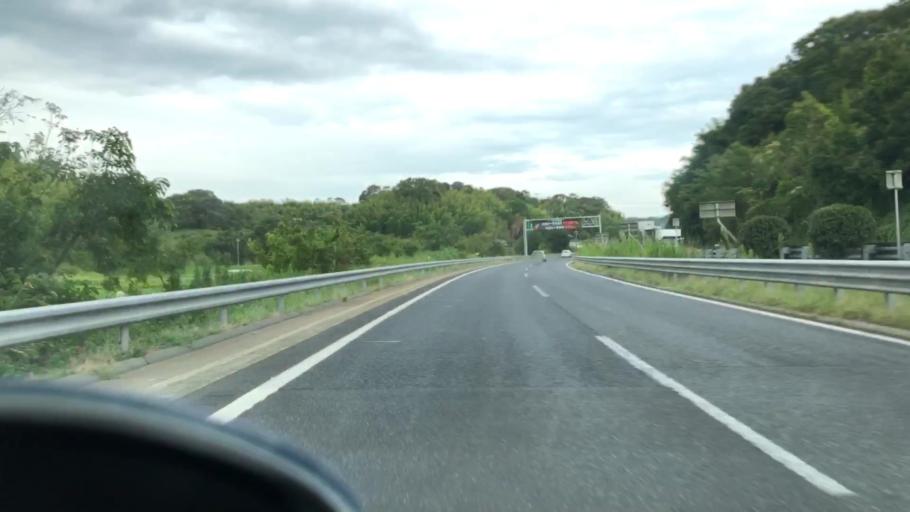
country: JP
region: Hyogo
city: Sandacho
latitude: 34.8912
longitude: 135.1390
